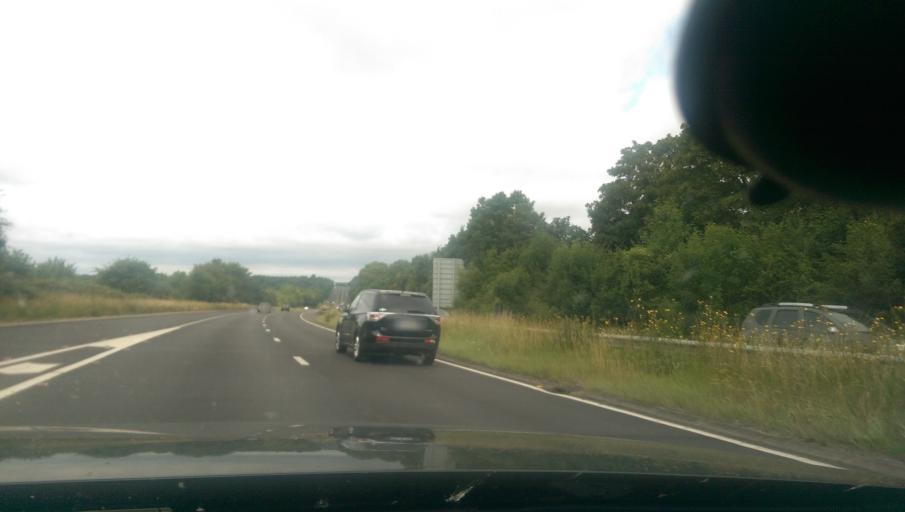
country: GB
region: England
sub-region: Hampshire
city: Andover
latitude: 51.1947
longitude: -1.4856
